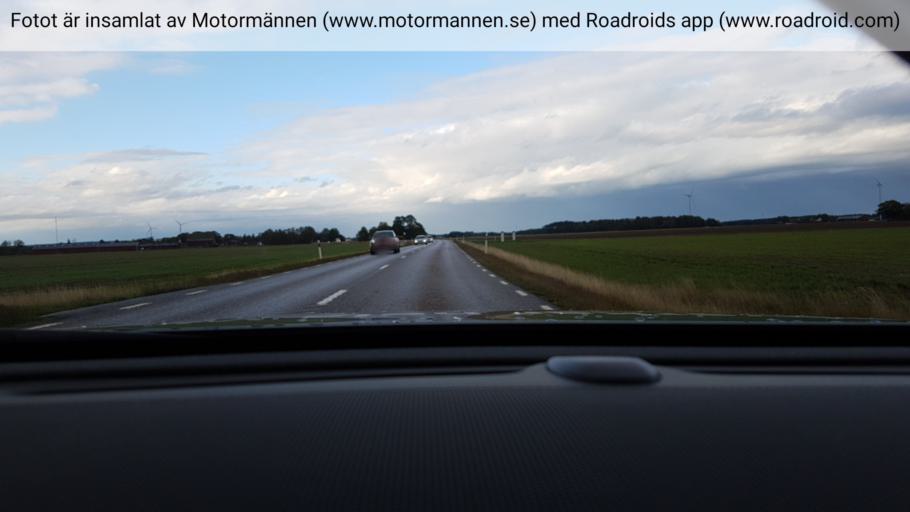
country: SE
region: Vaestra Goetaland
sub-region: Vanersborgs Kommun
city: Bralanda
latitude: 58.6214
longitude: 12.4164
